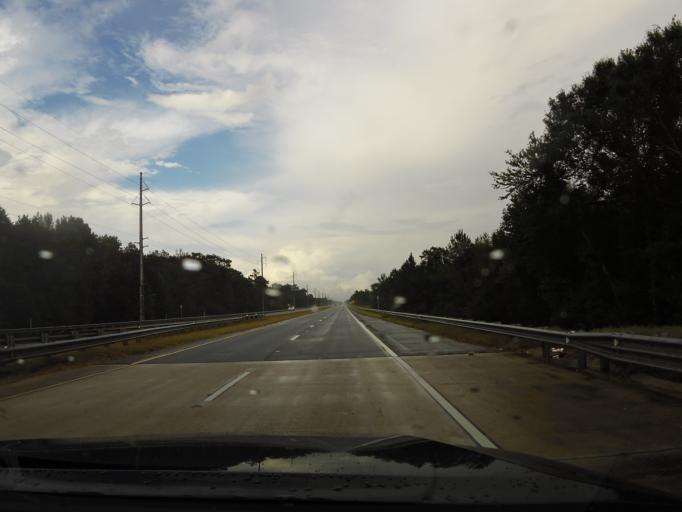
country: US
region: Georgia
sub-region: Long County
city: Ludowici
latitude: 31.6866
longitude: -81.7953
